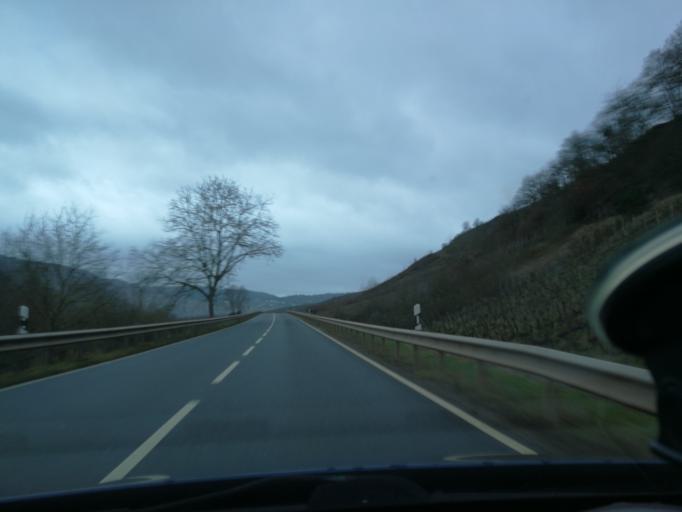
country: DE
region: Rheinland-Pfalz
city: Neumagen-Dhron
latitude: 49.8448
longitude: 6.8906
